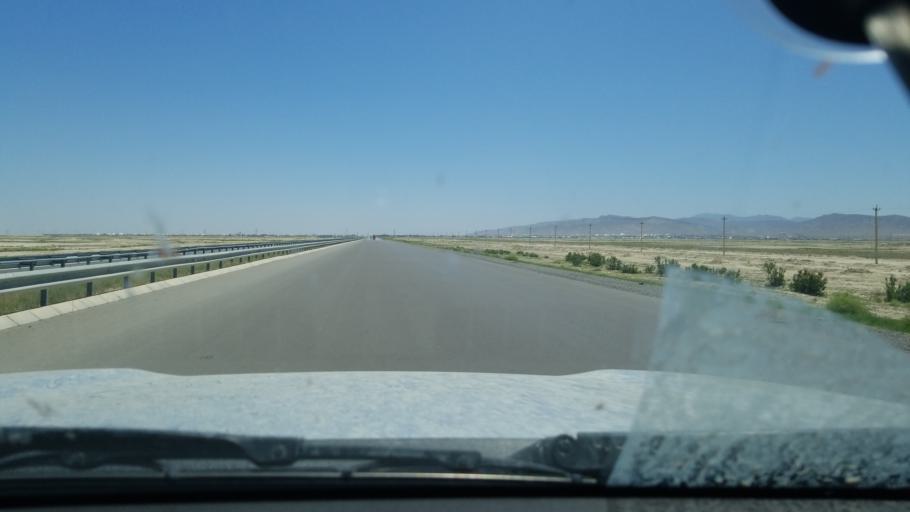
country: TM
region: Balkan
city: Serdar
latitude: 39.0179
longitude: 56.2163
